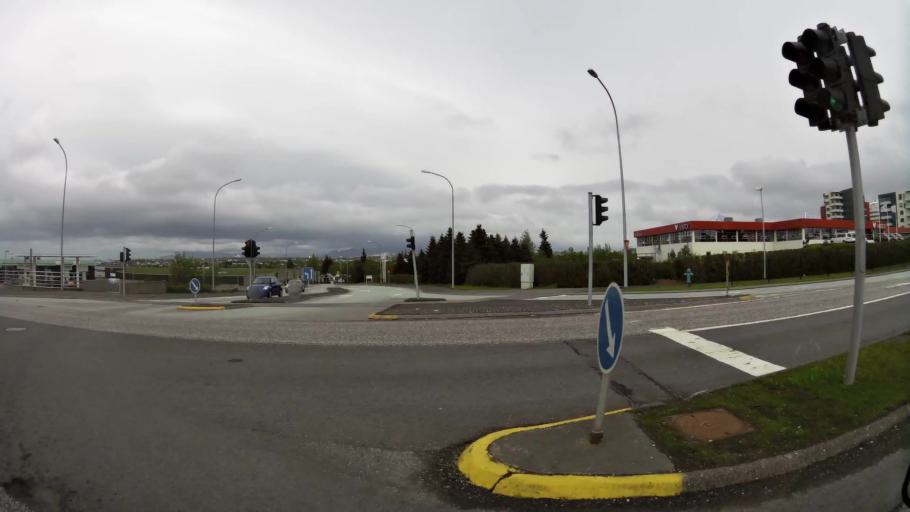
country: IS
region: Capital Region
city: Gardabaer
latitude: 64.0893
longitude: -21.9253
